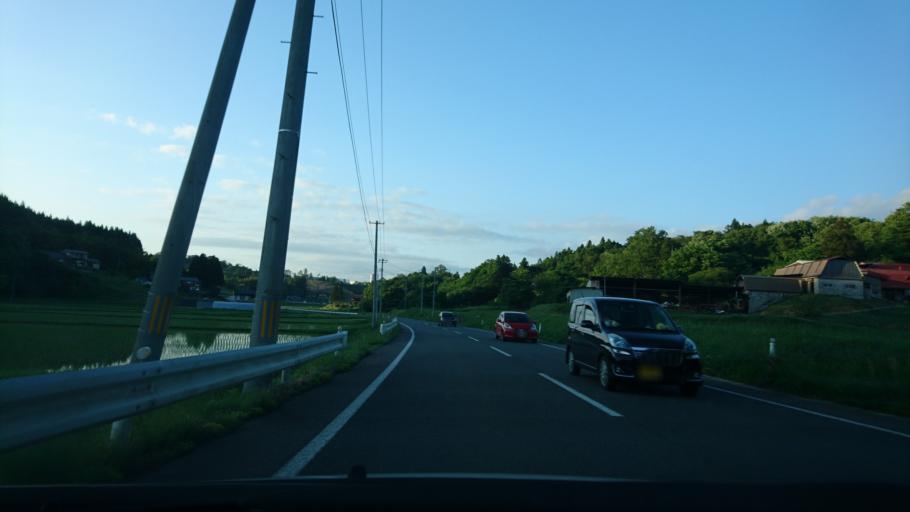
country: JP
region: Iwate
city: Ichinoseki
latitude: 38.8939
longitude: 141.1590
